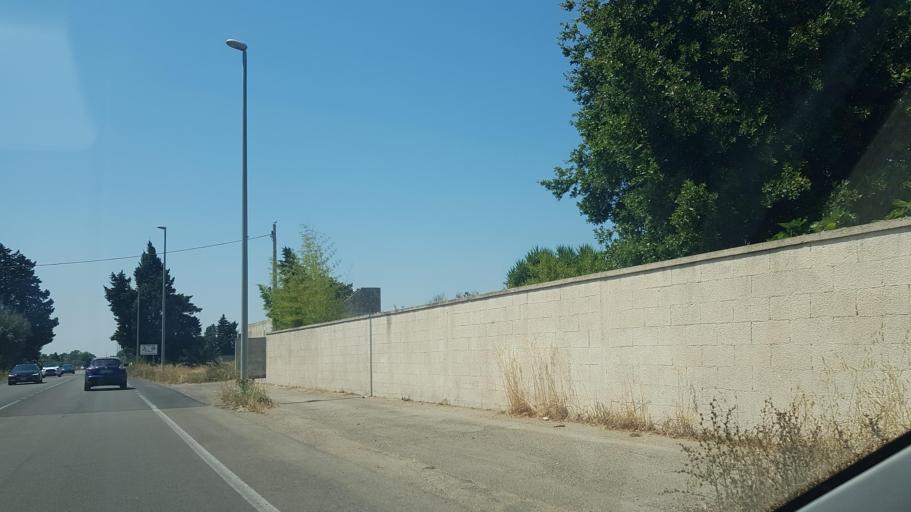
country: IT
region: Apulia
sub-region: Provincia di Lecce
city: Merine
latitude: 40.3385
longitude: 18.2273
